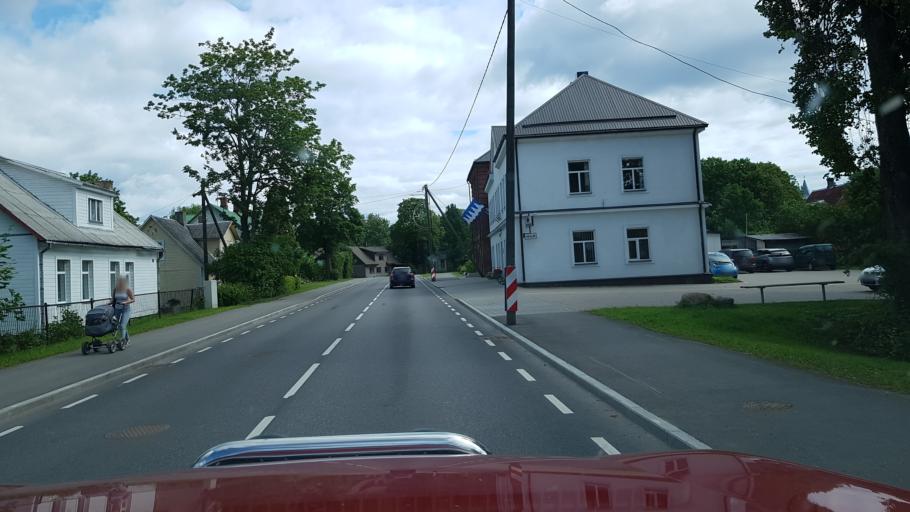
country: EE
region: Jogevamaa
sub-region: Mustvee linn
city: Mustvee
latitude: 58.8482
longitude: 26.9366
